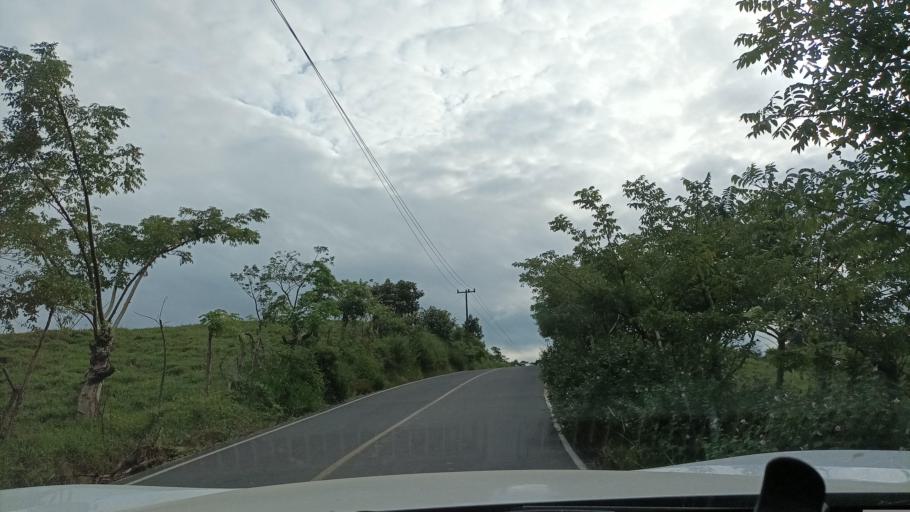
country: MX
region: Veracruz
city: Hidalgotitlan
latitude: 17.6902
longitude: -94.4600
